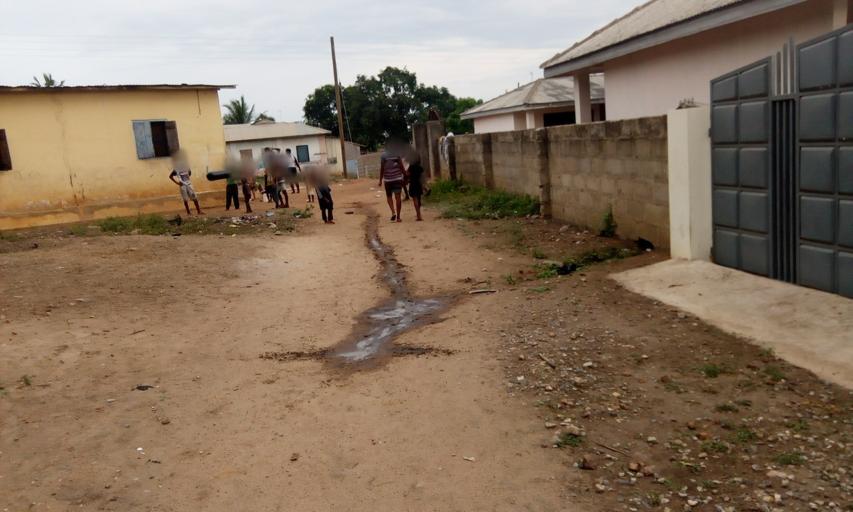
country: GH
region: Central
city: Winneba
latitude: 5.3581
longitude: -0.6288
